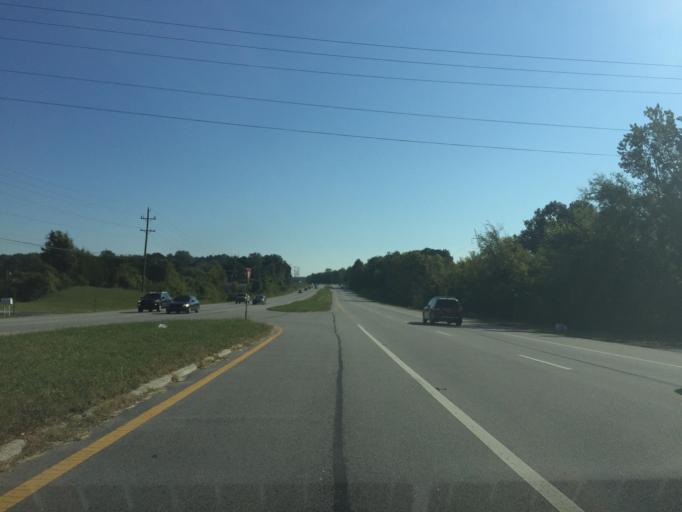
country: US
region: Tennessee
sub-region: Hamilton County
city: Harrison
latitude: 35.1061
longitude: -85.1536
